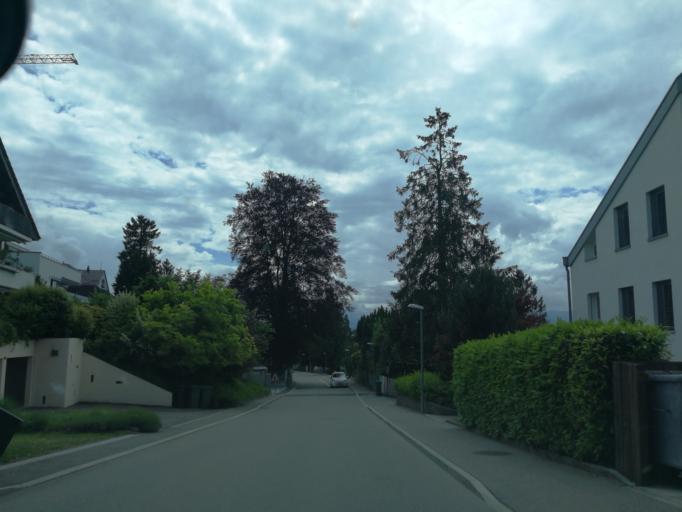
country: CH
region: Zurich
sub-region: Bezirk Meilen
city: Herrliberg
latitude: 47.2896
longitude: 8.6166
